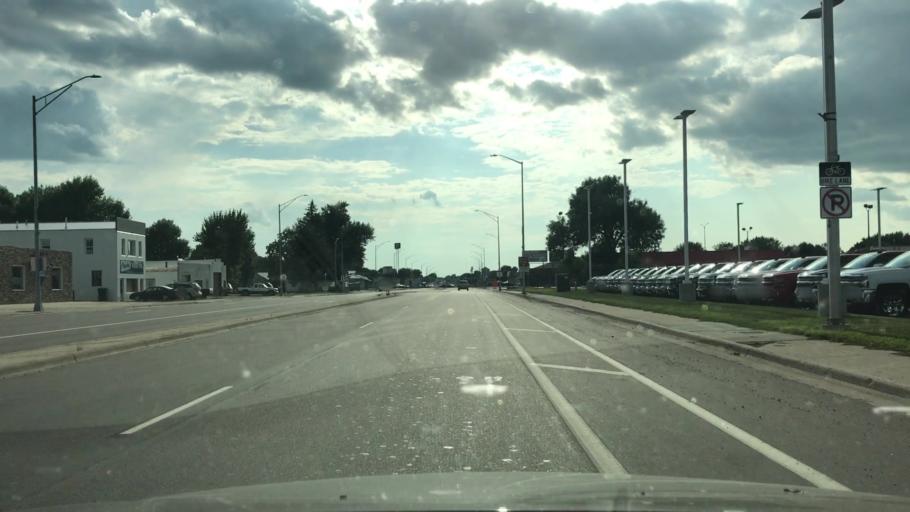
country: US
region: Minnesota
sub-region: Nobles County
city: Worthington
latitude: 43.6312
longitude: -95.5865
